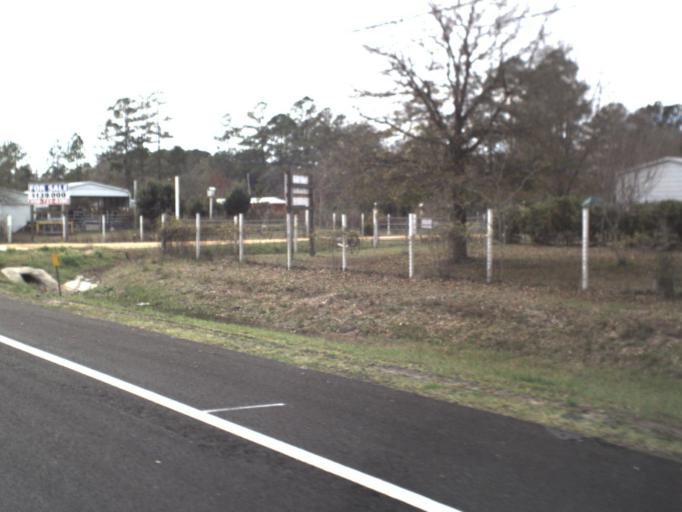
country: US
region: Florida
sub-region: Bay County
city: Youngstown
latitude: 30.3238
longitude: -85.4517
